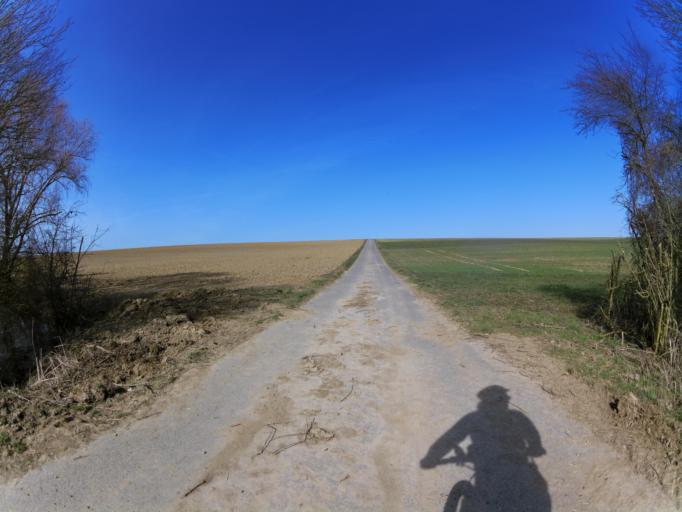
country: DE
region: Bavaria
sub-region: Regierungsbezirk Unterfranken
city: Prosselsheim
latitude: 49.8333
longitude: 10.1288
